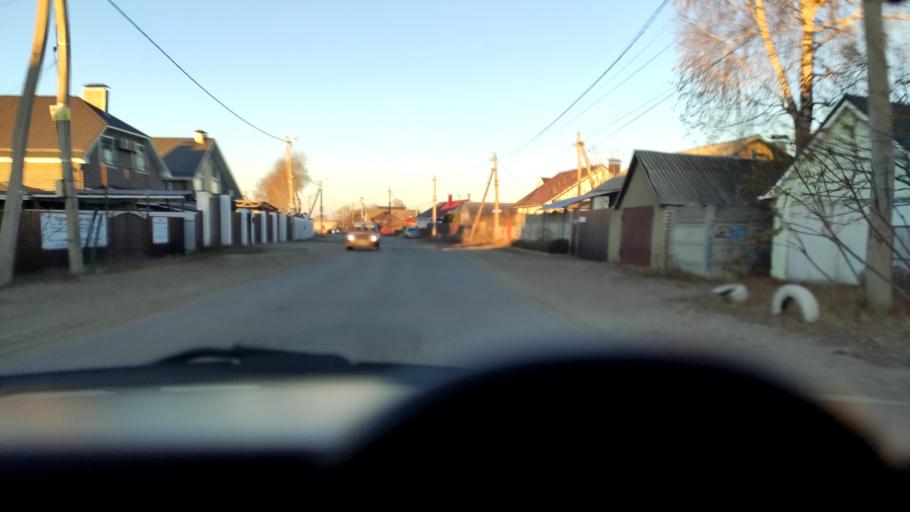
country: RU
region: Voronezj
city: Podgornoye
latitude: 51.7393
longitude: 39.1532
